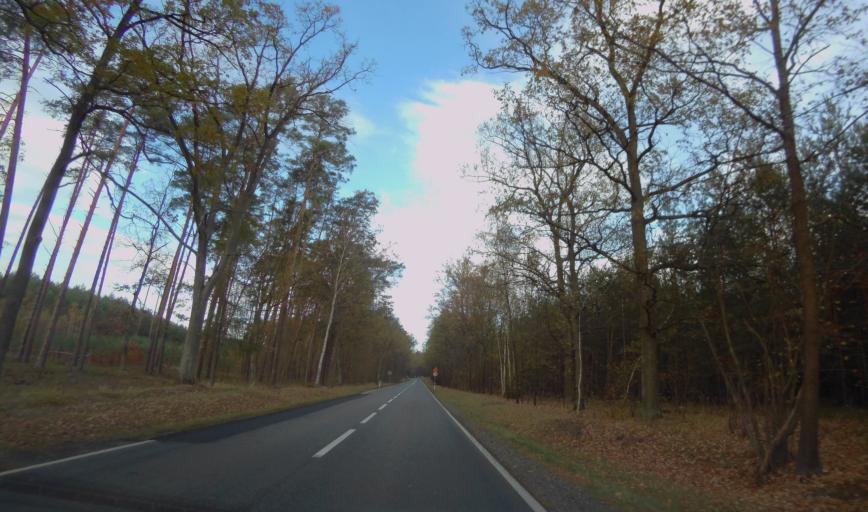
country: PL
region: Subcarpathian Voivodeship
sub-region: Powiat nizanski
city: Krzeszow
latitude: 50.3815
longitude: 22.3095
